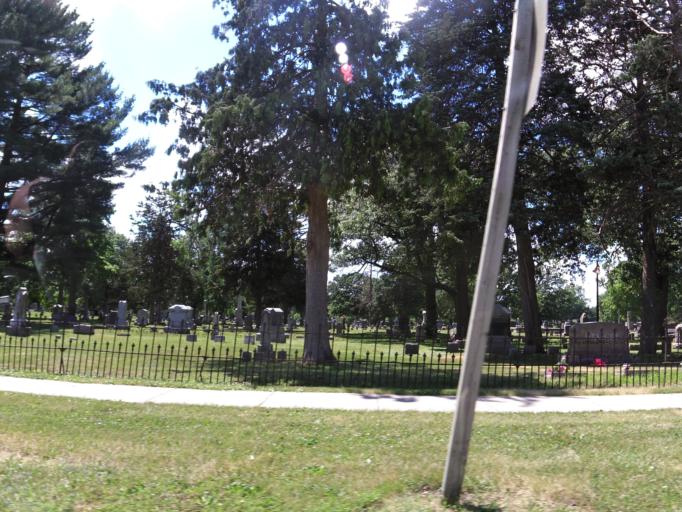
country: US
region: Iowa
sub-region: Buchanan County
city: Independence
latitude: 42.4630
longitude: -91.8917
